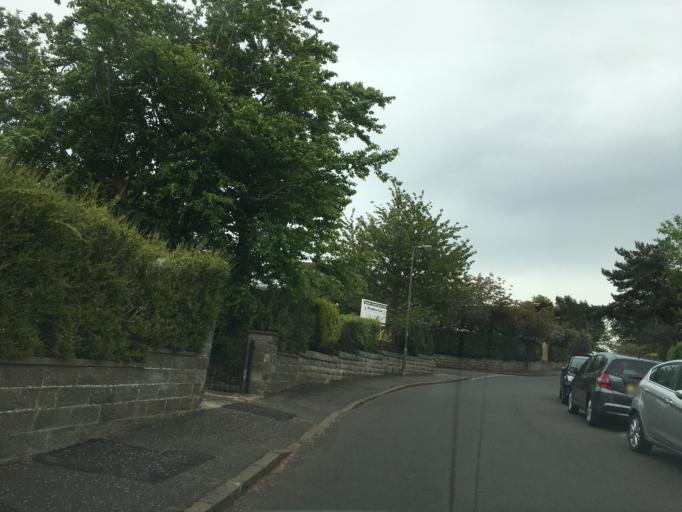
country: GB
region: Scotland
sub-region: Edinburgh
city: Edinburgh
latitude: 55.9152
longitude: -3.2065
